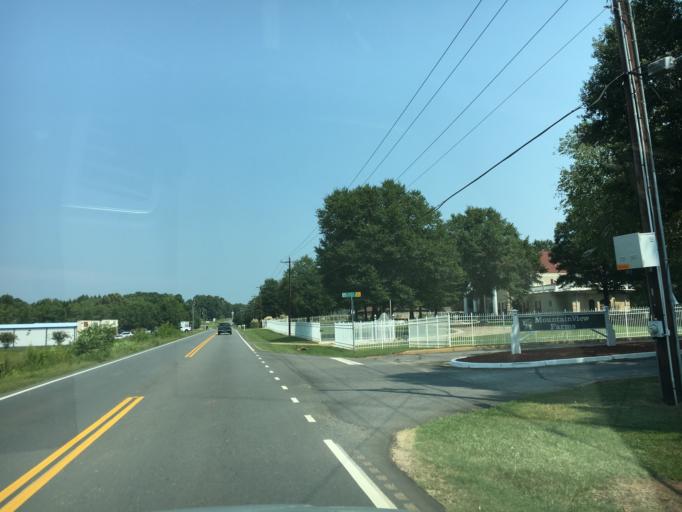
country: US
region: South Carolina
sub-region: Spartanburg County
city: Valley Falls
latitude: 35.0347
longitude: -81.9473
